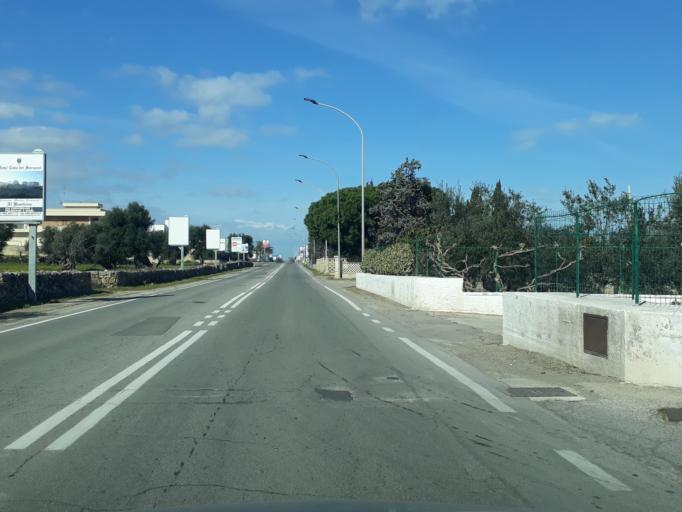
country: IT
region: Apulia
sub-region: Provincia di Bari
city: Monopoli
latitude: 40.9672
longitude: 17.2711
